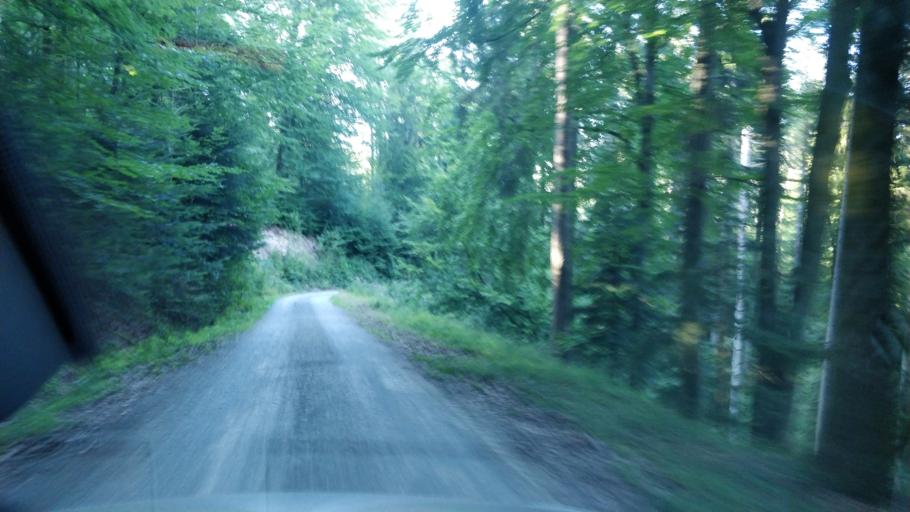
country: DE
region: Baden-Wuerttemberg
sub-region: Regierungsbezirk Stuttgart
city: Murrhardt
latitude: 49.0115
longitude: 9.5728
